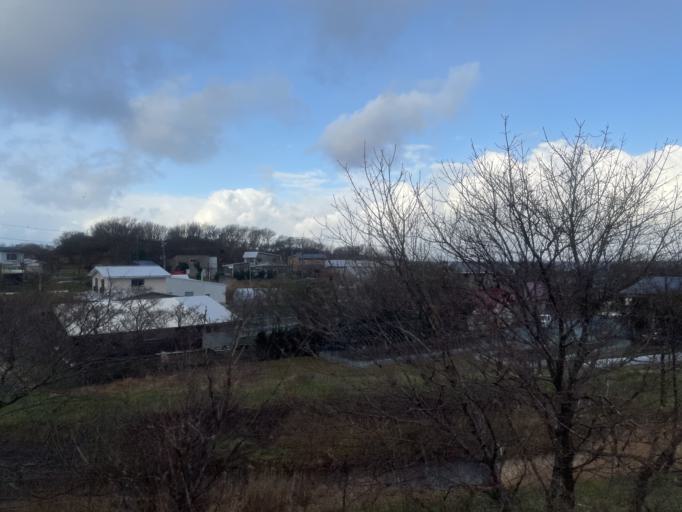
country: JP
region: Aomori
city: Misawa
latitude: 40.9197
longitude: 141.1942
